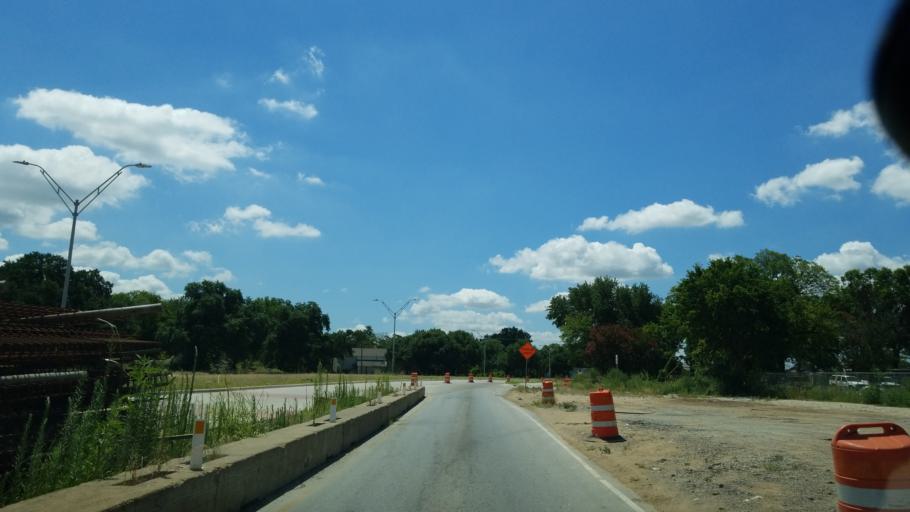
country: US
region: Texas
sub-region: Dallas County
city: Dallas
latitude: 32.7453
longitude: -96.7585
